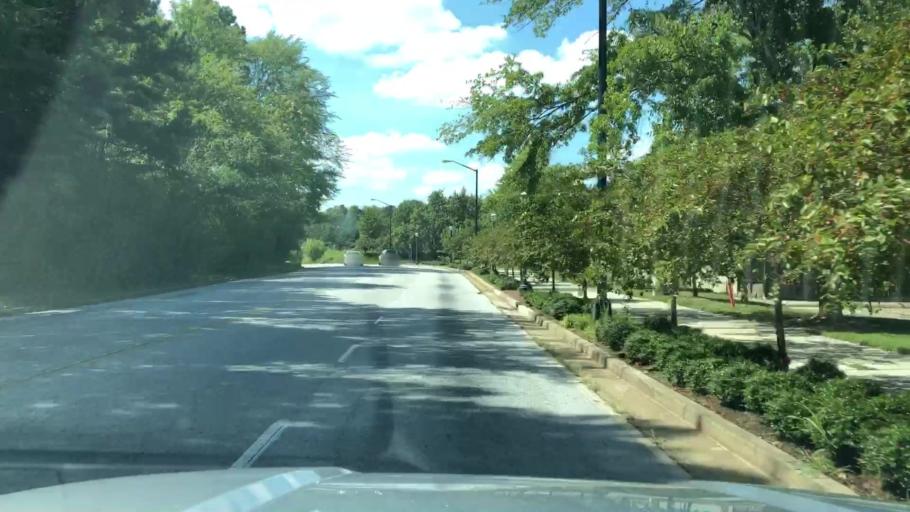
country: US
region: Georgia
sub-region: Fulton County
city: East Point
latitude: 33.6864
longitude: -84.4953
